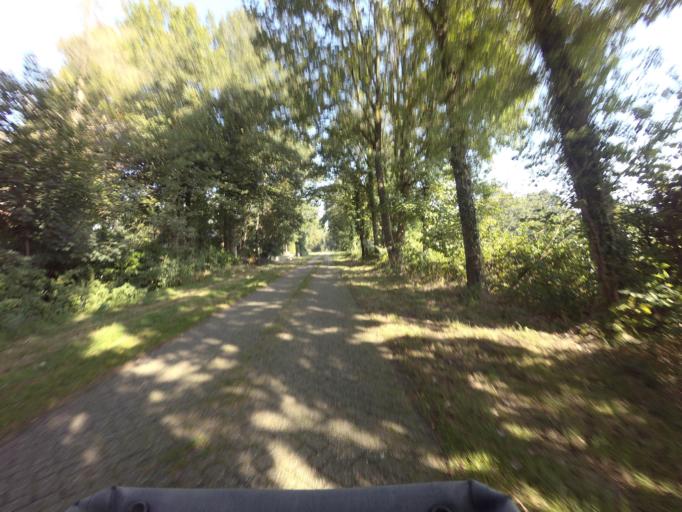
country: DE
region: Lower Saxony
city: Laar
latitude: 52.5947
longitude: 6.7791
